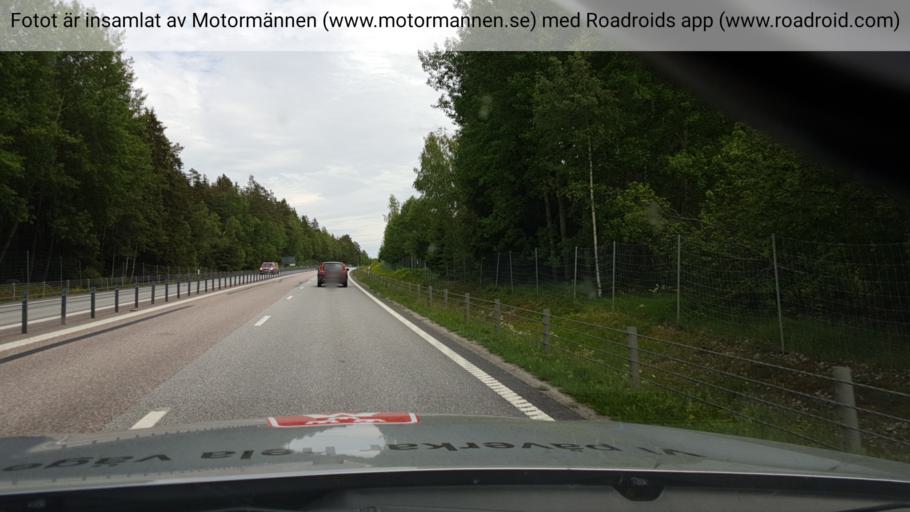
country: SE
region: Vaestmanland
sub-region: Kopings Kommun
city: Koping
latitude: 59.5733
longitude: 16.1018
